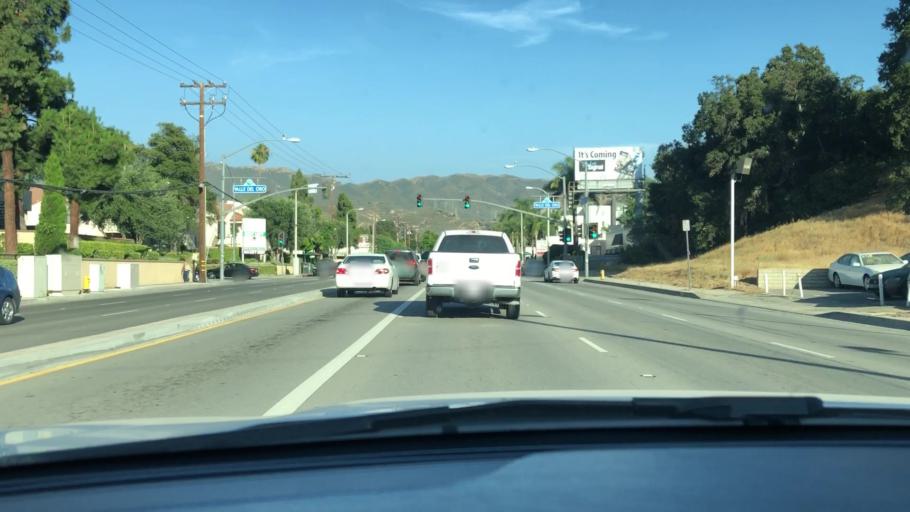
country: US
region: California
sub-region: Los Angeles County
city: Santa Clarita
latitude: 34.3712
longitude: -118.5154
